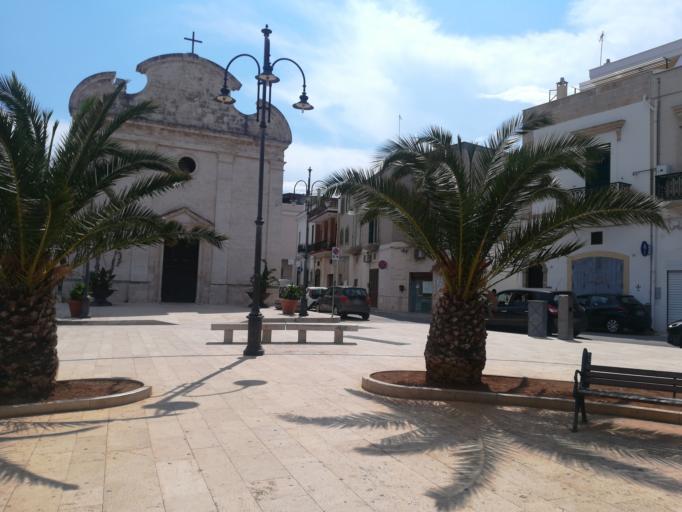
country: IT
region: Apulia
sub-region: Provincia di Bari
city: Polignano a Mare
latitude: 40.9945
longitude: 17.2224
